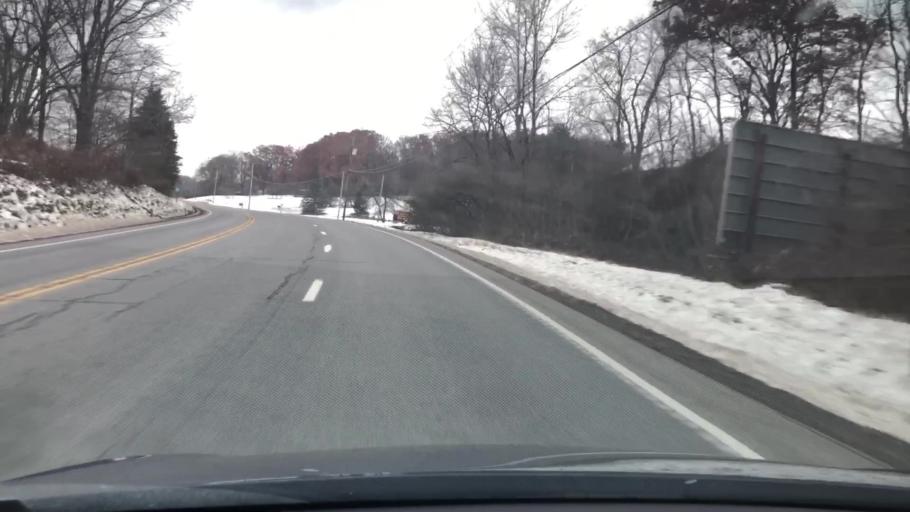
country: US
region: Pennsylvania
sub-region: Jefferson County
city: Brookville
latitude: 41.1493
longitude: -79.1241
